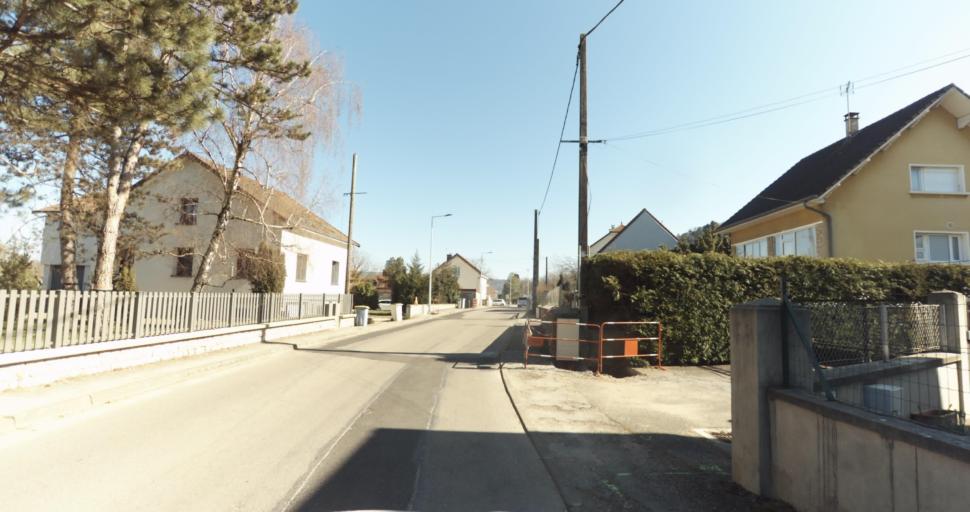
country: FR
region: Franche-Comte
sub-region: Departement du Jura
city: Montmorot
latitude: 46.6743
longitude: 5.5285
